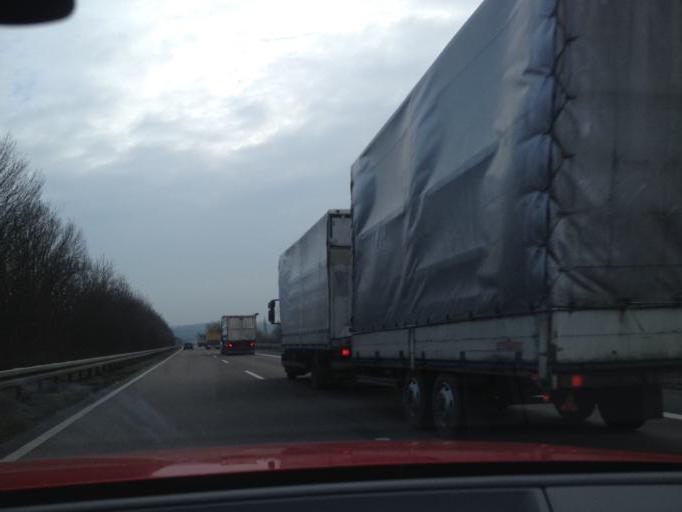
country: DE
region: Hesse
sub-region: Regierungsbezirk Darmstadt
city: Altenstadt
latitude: 50.2862
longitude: 8.9696
